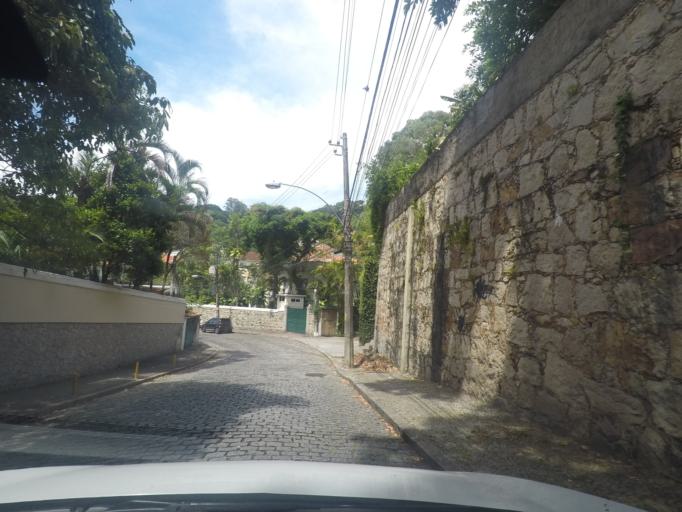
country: BR
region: Rio de Janeiro
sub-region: Rio De Janeiro
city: Rio de Janeiro
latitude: -22.9295
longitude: -43.1888
